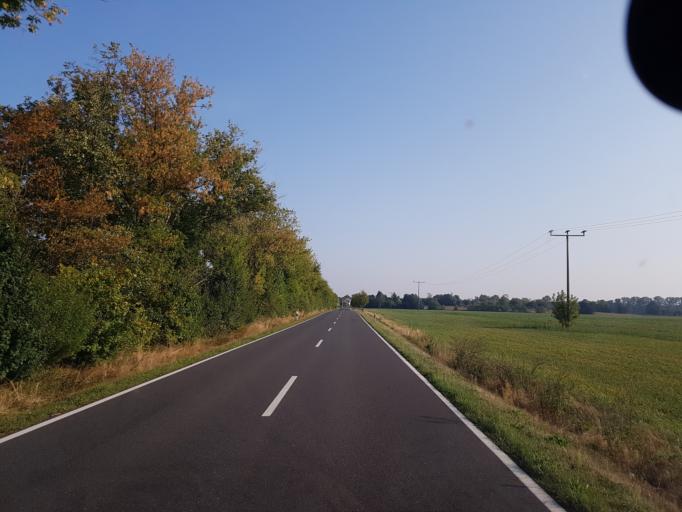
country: DE
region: Brandenburg
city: Finsterwalde
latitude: 51.6588
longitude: 13.7352
